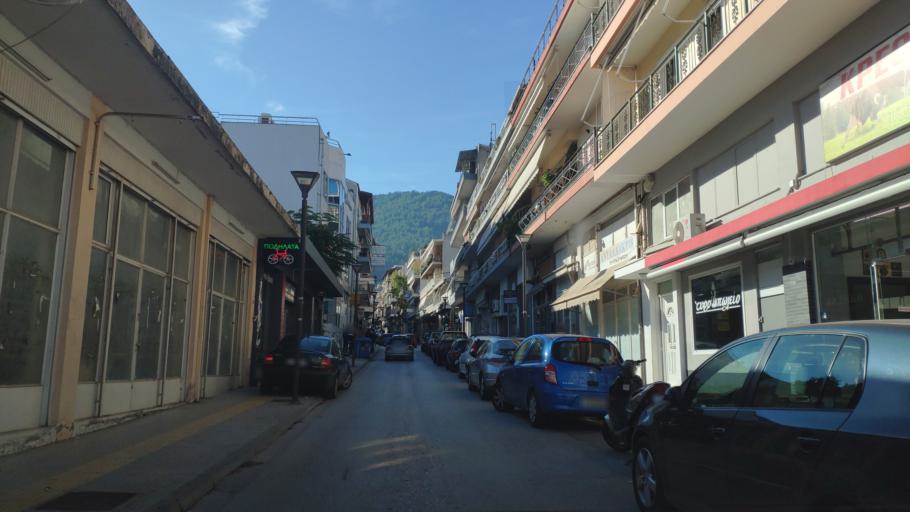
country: GR
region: Central Greece
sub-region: Nomos Voiotias
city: Livadeia
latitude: 38.4400
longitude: 22.8776
